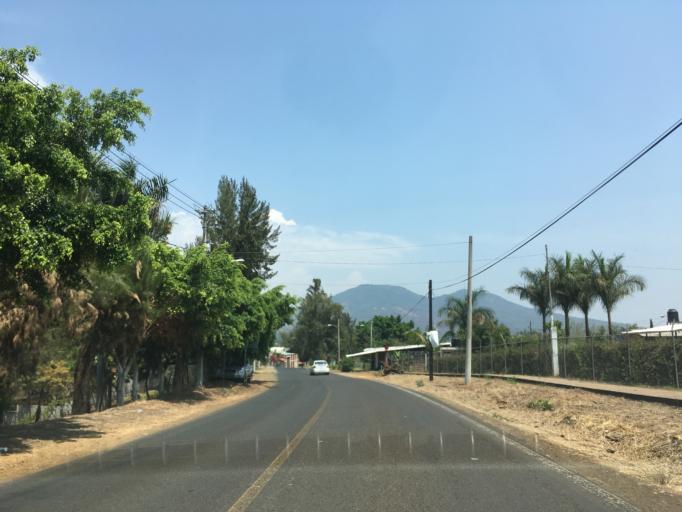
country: MX
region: Michoacan
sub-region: Ziracuaretiro
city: Patuan
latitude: 19.4216
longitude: -101.9217
